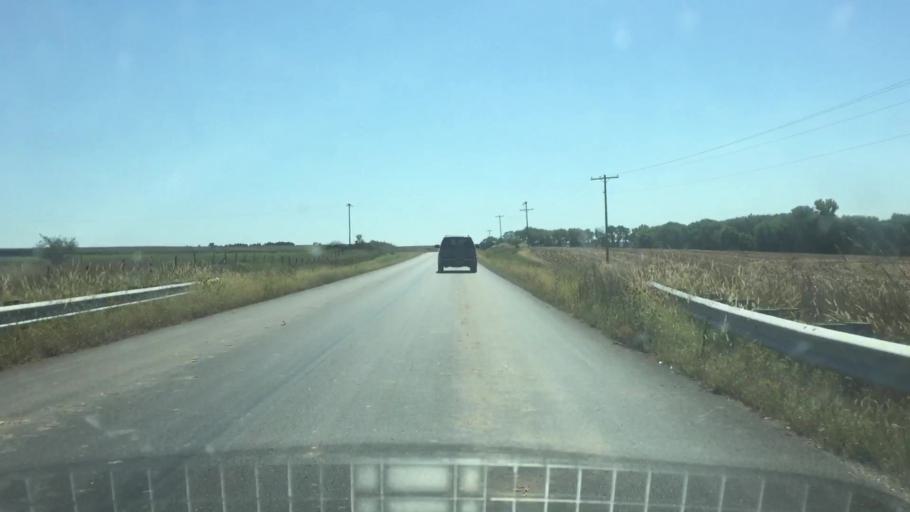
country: US
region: Kansas
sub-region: Marshall County
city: Marysville
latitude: 39.8814
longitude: -96.6010
